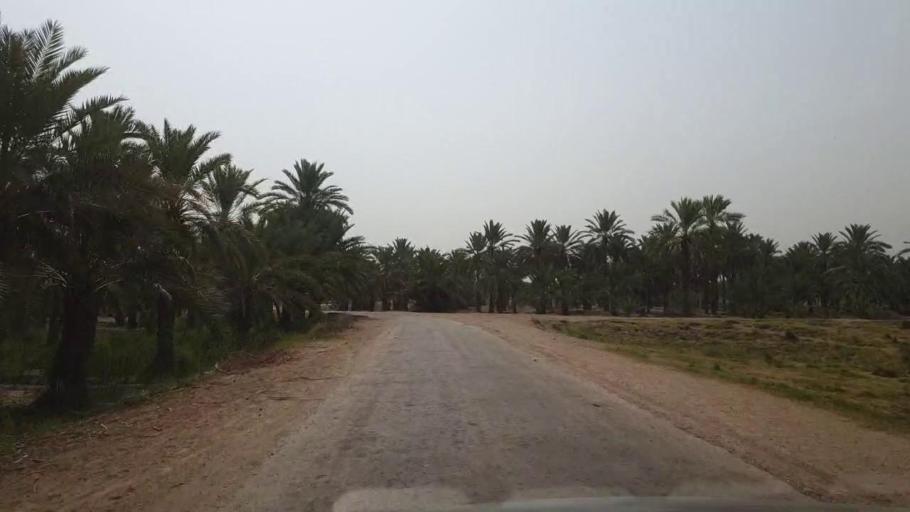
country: PK
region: Sindh
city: Gambat
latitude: 27.4159
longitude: 68.5498
